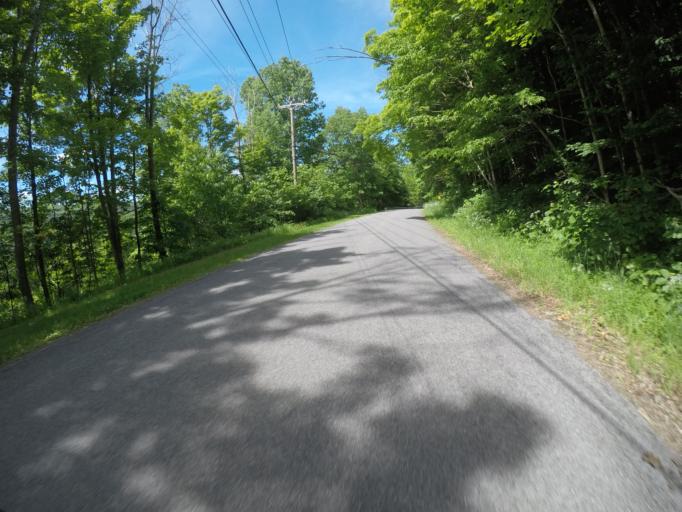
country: US
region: New York
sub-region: Delaware County
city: Stamford
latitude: 42.1450
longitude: -74.6491
